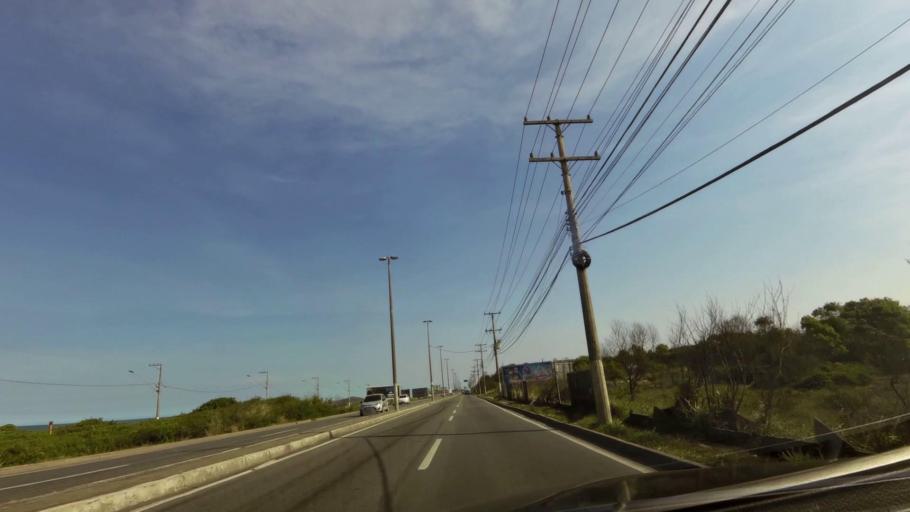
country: BR
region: Espirito Santo
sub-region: Vila Velha
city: Vila Velha
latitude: -20.3857
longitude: -40.3120
